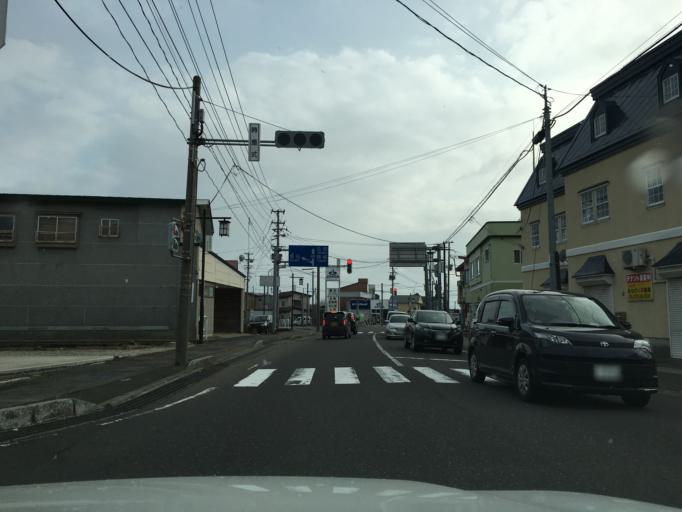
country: JP
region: Aomori
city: Namioka
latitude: 40.7115
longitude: 140.5900
